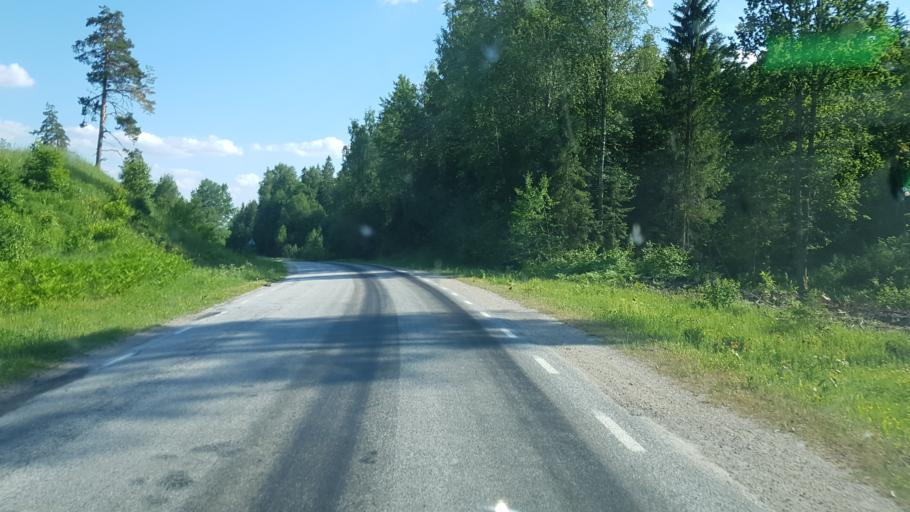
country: EE
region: Vorumaa
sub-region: Voru linn
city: Voru
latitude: 57.7481
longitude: 26.9163
